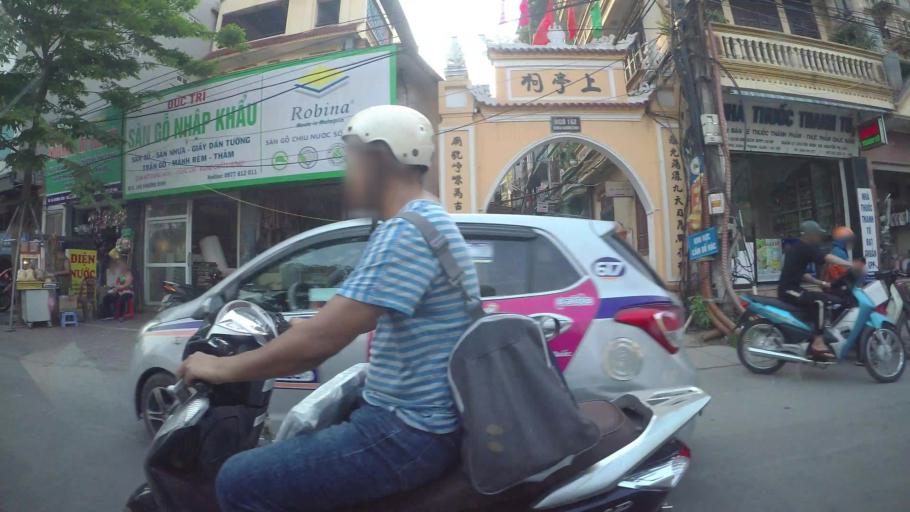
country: VN
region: Ha Noi
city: Thanh Xuan
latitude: 20.9942
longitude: 105.8142
